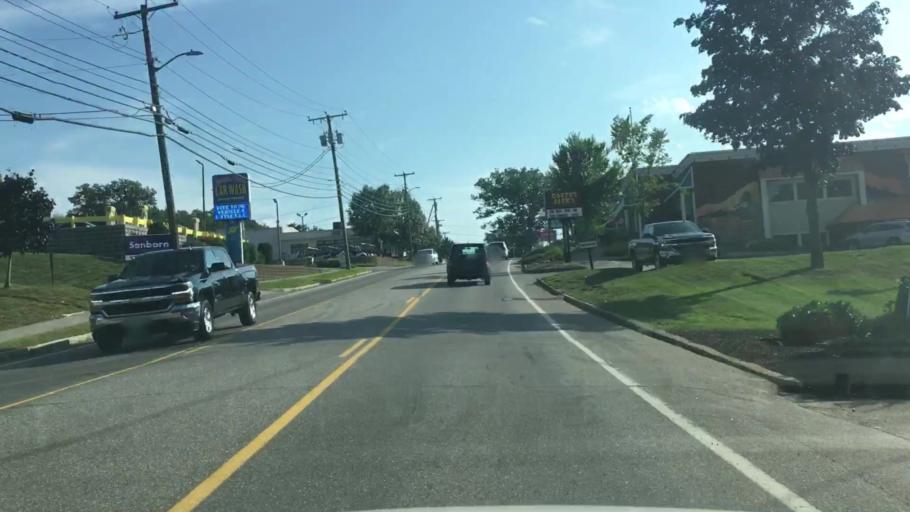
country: US
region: New Hampshire
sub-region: Belknap County
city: Laconia
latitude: 43.5583
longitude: -71.4544
